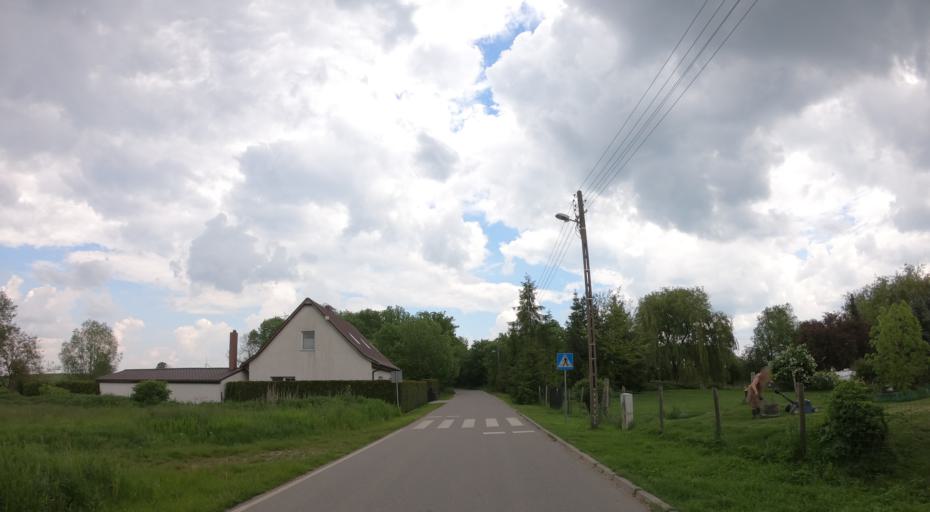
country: PL
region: West Pomeranian Voivodeship
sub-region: Powiat pyrzycki
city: Bielice
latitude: 53.1359
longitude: 14.7549
